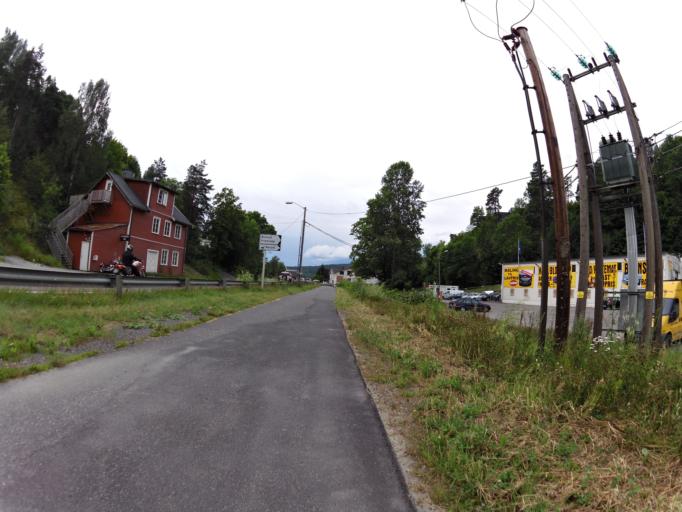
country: NO
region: Akershus
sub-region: As
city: As
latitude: 59.7304
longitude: 10.7354
